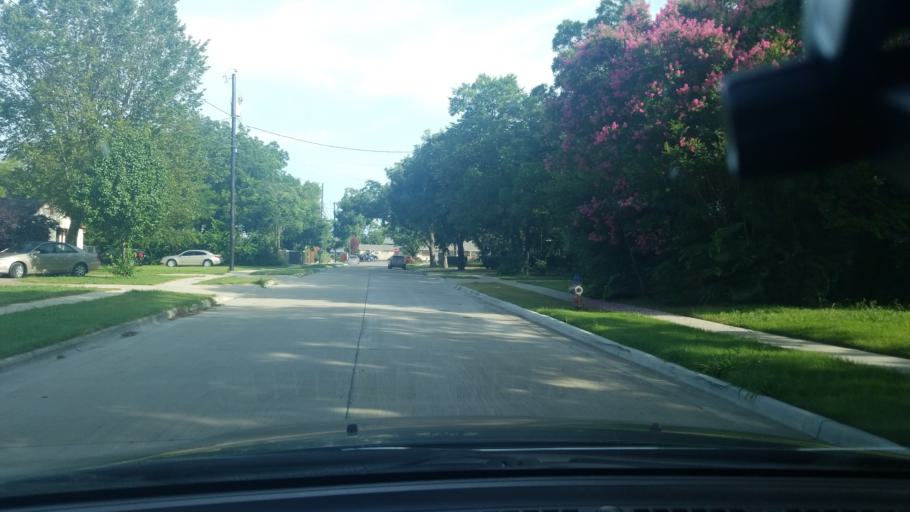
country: US
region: Texas
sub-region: Dallas County
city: Highland Park
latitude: 32.8001
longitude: -96.7136
